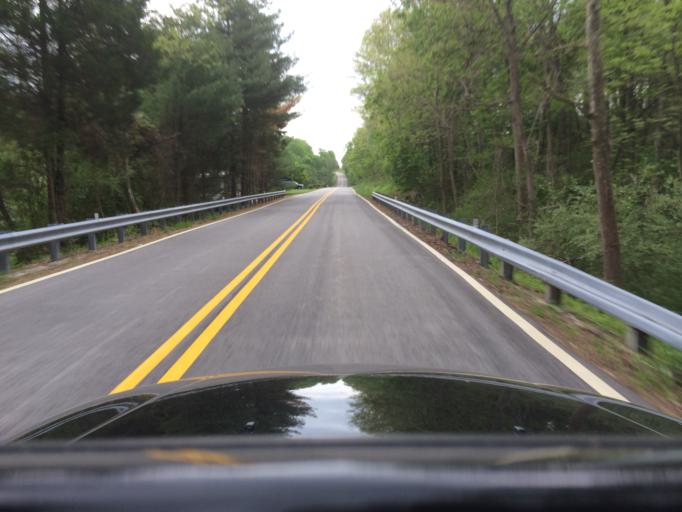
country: US
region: Maryland
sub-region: Carroll County
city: Eldersburg
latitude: 39.4613
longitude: -77.0014
